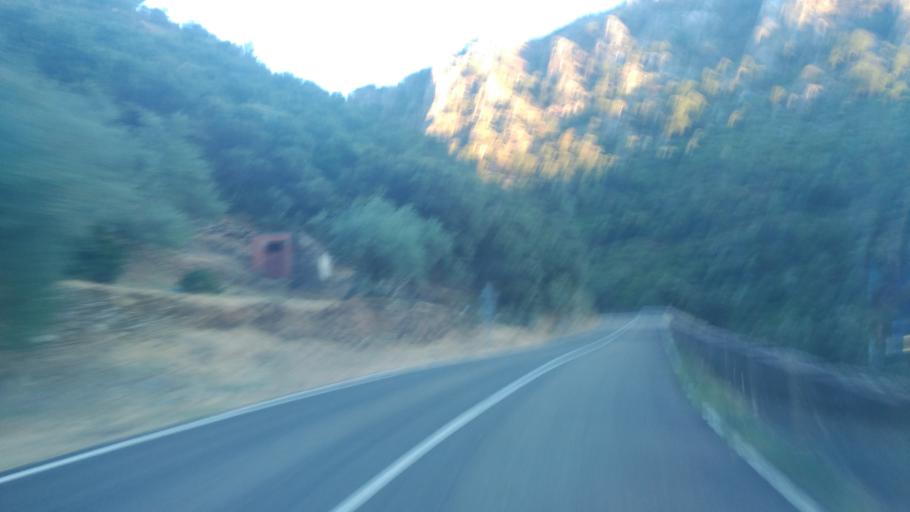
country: ES
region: Castille and Leon
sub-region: Provincia de Salamanca
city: Mieza
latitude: 41.1890
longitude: -6.6797
